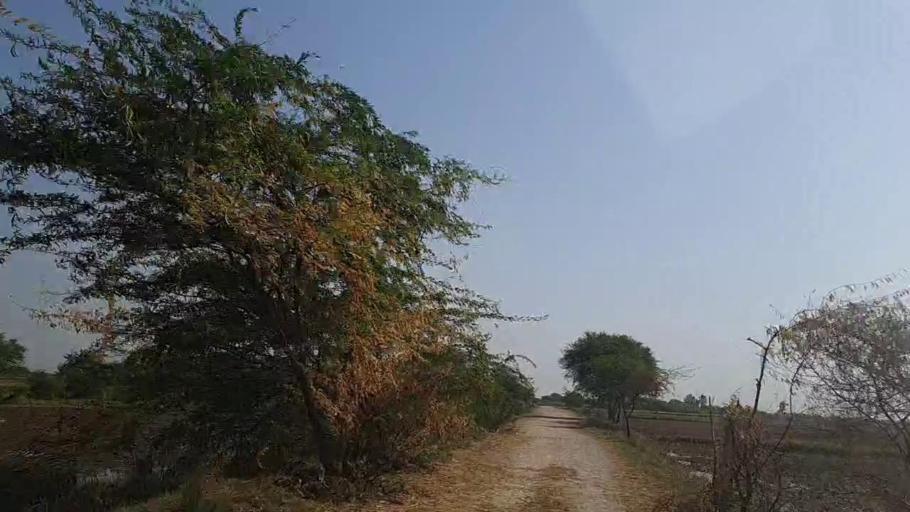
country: PK
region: Sindh
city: Daro Mehar
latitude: 24.7203
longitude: 68.1109
